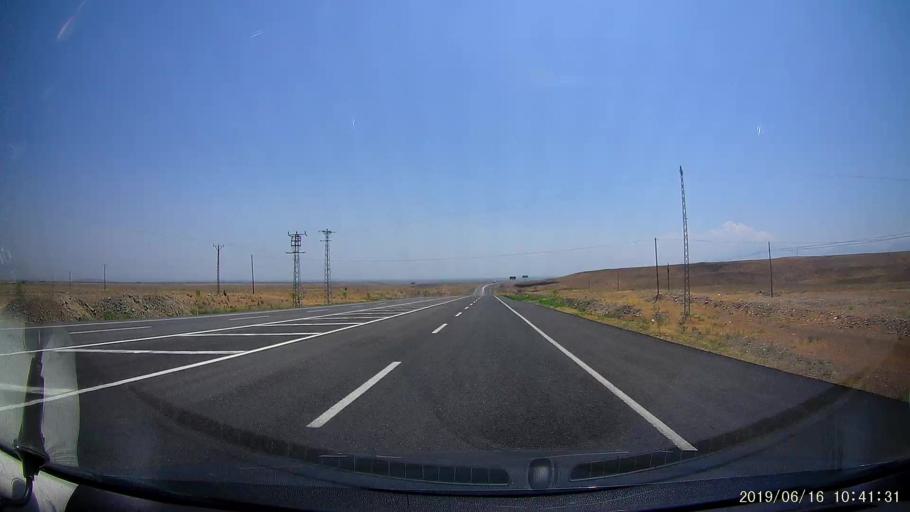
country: TR
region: Igdir
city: Tuzluca
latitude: 40.0471
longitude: 43.7847
